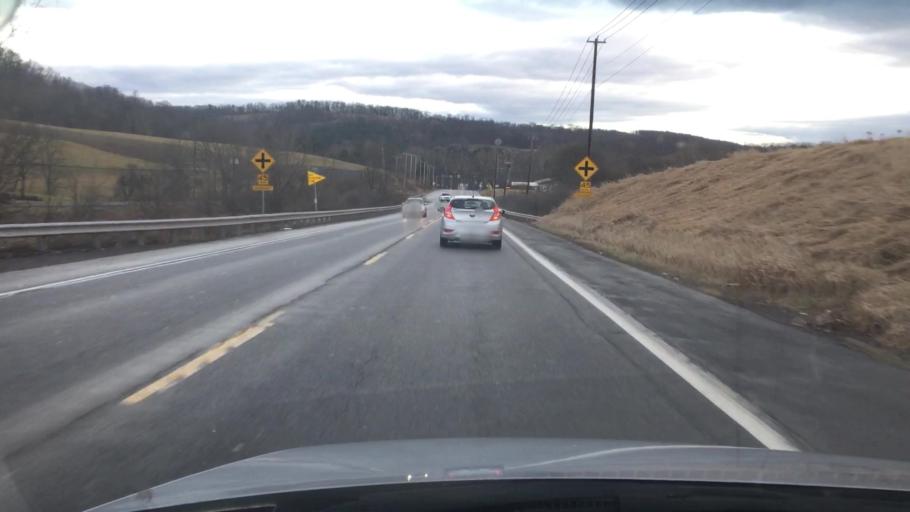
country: US
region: Pennsylvania
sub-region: Columbia County
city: Bloomsburg
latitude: 41.0230
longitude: -76.4860
